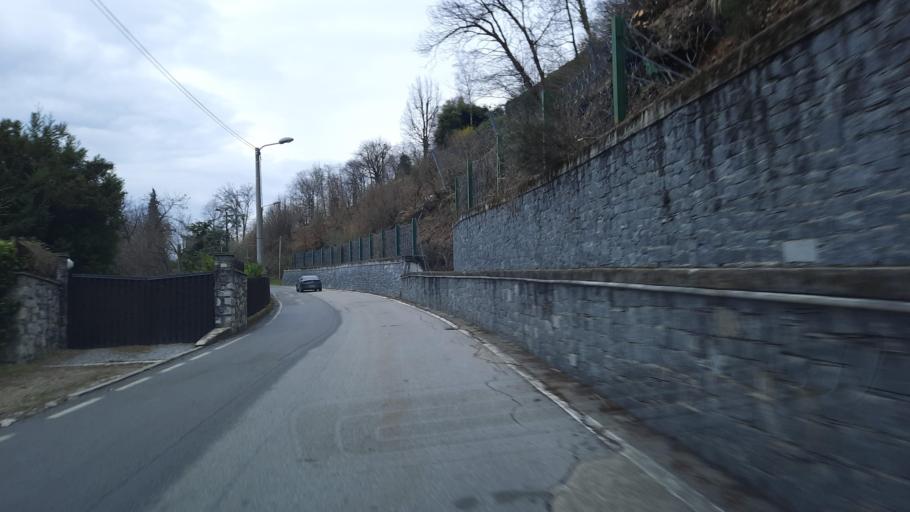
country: IT
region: Piedmont
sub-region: Provincia di Novara
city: Pella
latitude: 45.8085
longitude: 8.3849
